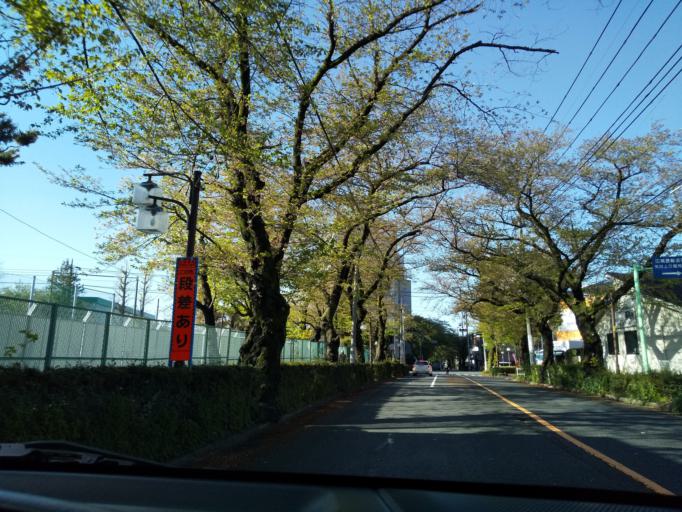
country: JP
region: Tokyo
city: Hino
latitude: 35.6878
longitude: 139.4337
